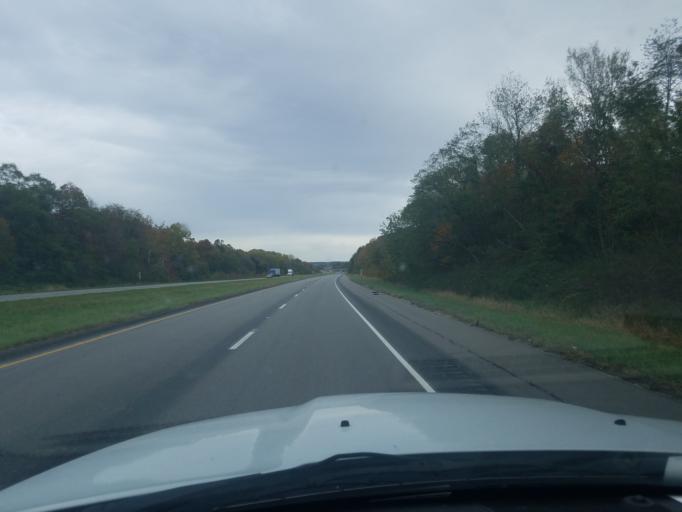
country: US
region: Indiana
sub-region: Spencer County
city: Dale
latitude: 38.2005
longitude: -87.1025
